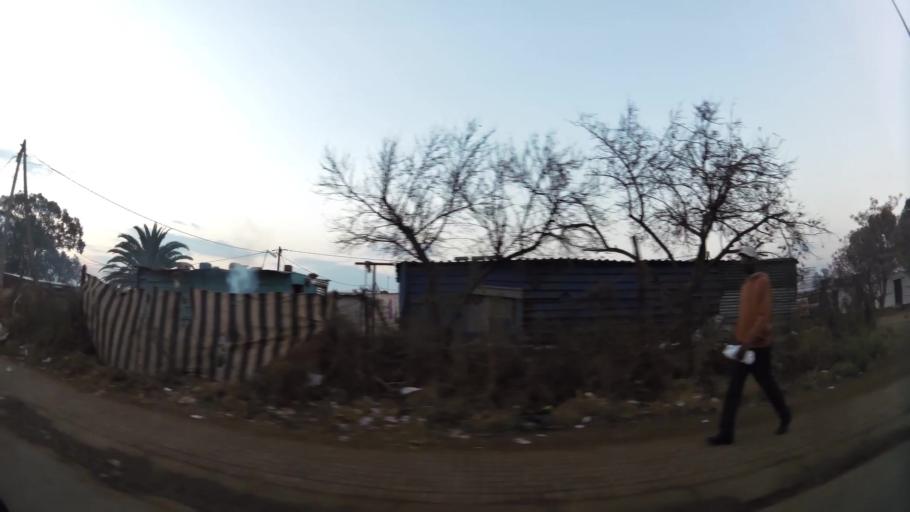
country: ZA
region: Gauteng
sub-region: City of Johannesburg Metropolitan Municipality
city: Orange Farm
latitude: -26.5547
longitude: 27.8563
